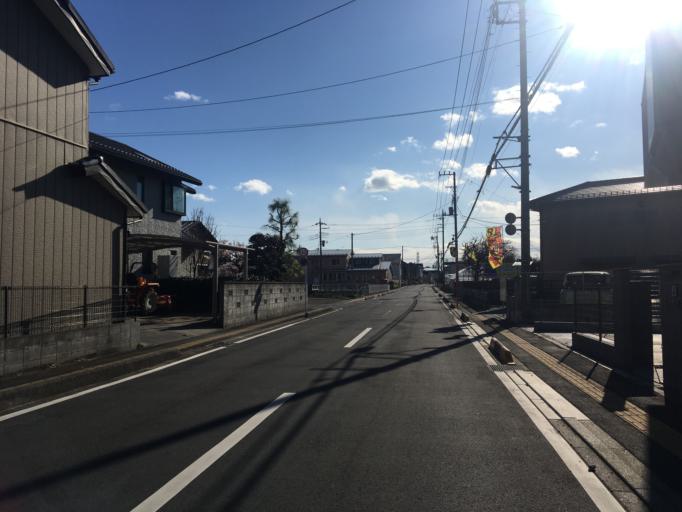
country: JP
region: Saitama
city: Shiki
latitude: 35.8254
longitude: 139.5655
